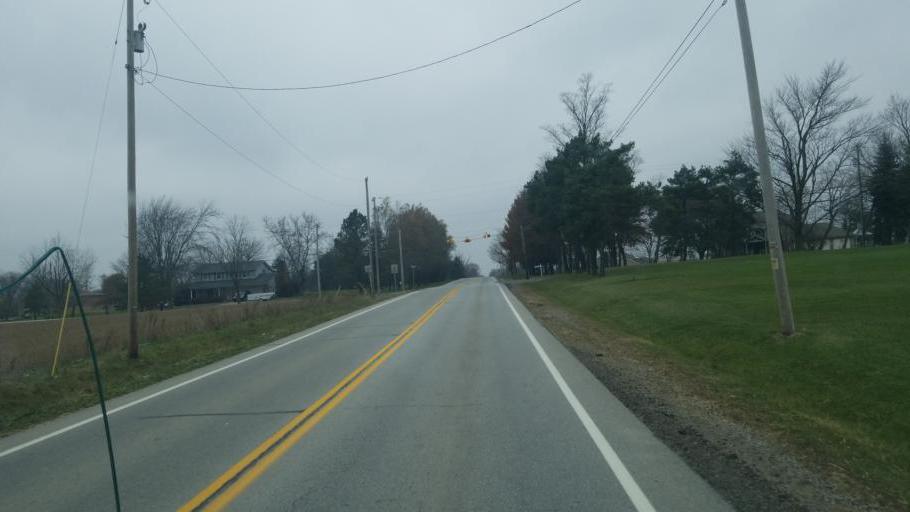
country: US
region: Ohio
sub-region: Medina County
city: Medina
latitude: 41.1539
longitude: -81.9252
